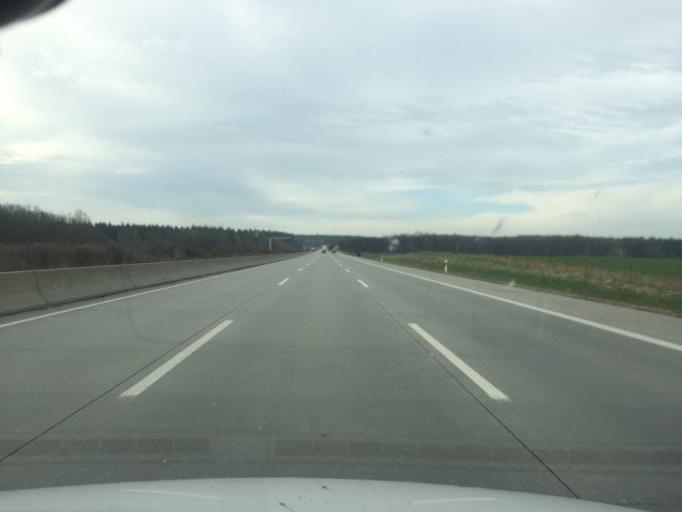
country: DE
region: Thuringia
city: Schwarzbach
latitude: 50.7970
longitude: 11.8952
